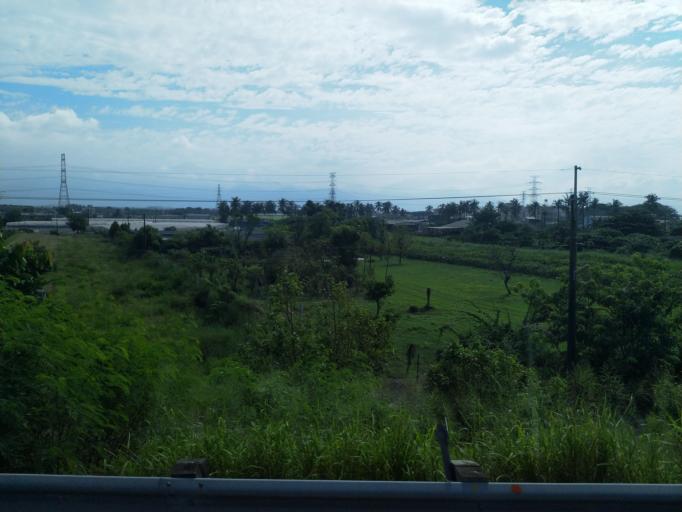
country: TW
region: Taiwan
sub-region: Pingtung
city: Pingtung
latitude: 22.8252
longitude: 120.4883
